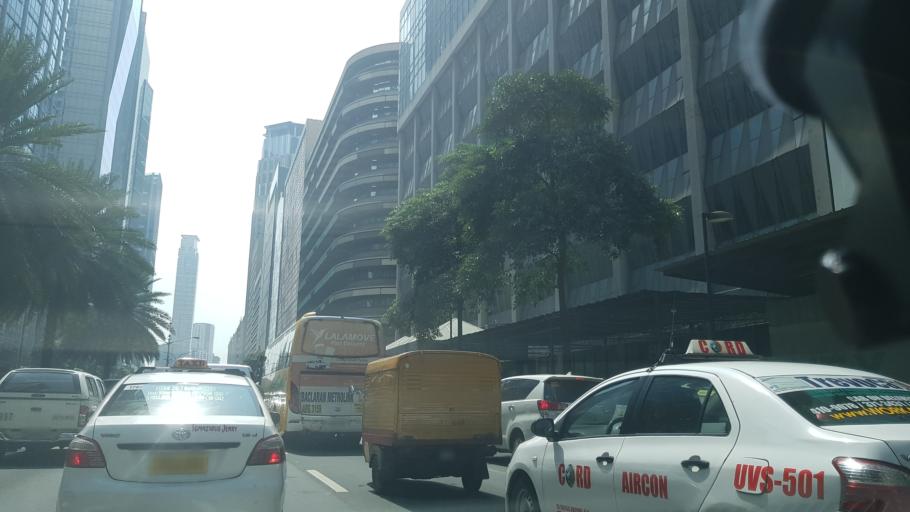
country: PH
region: Metro Manila
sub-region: Makati City
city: Makati City
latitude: 14.5588
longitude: 121.0184
